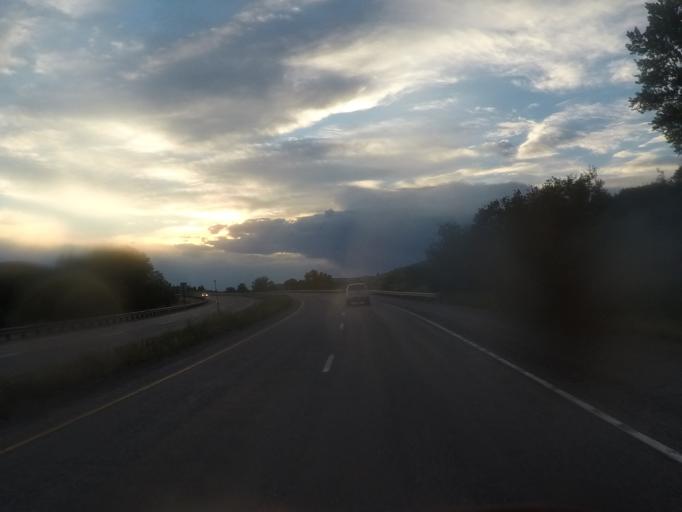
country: US
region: Montana
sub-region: Gallatin County
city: Bozeman
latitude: 45.6452
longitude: -110.9293
